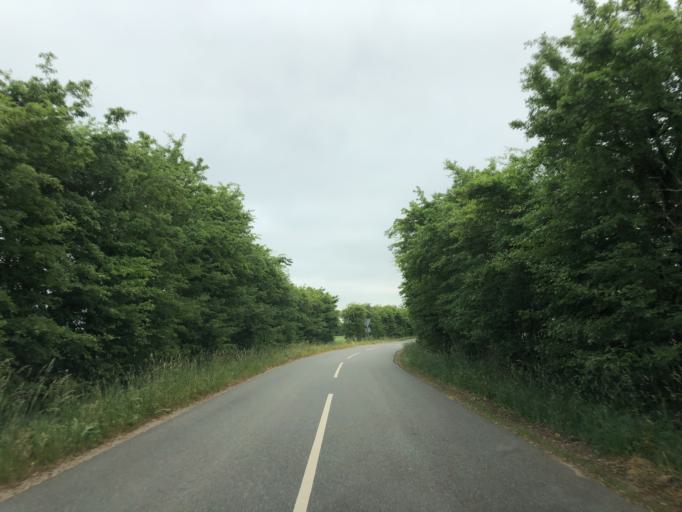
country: DK
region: Central Jutland
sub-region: Holstebro Kommune
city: Holstebro
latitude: 56.2411
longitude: 8.6104
